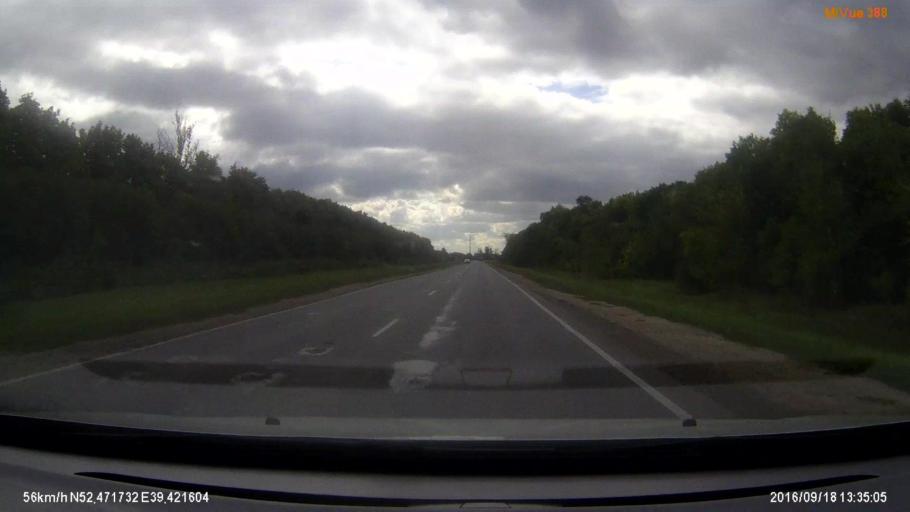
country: RU
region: Lipetsk
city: Borinskoye
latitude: 52.4944
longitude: 39.4501
